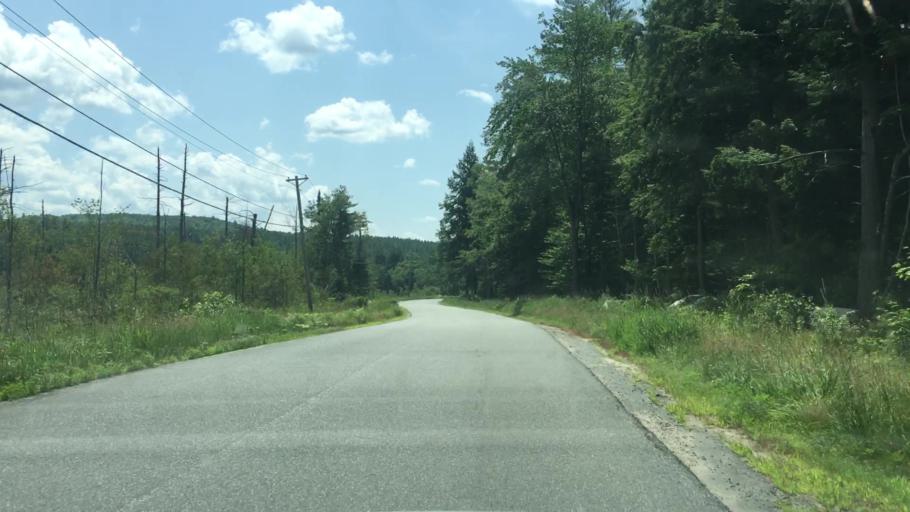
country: US
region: New Hampshire
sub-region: Grafton County
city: Enfield
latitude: 43.6823
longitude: -72.0934
